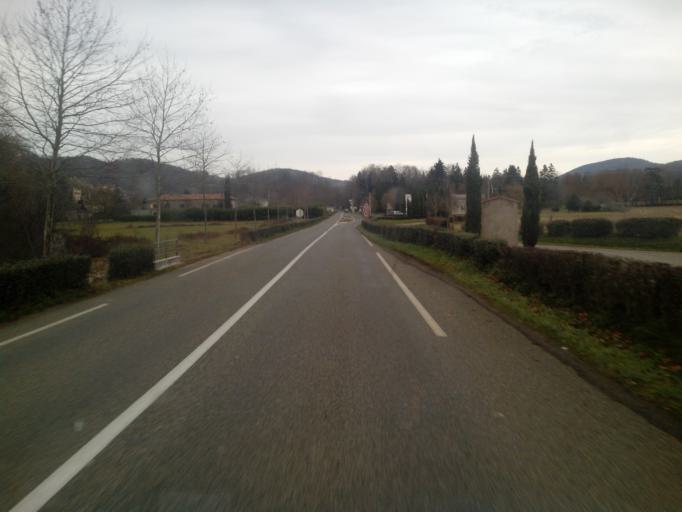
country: FR
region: Midi-Pyrenees
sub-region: Departement de l'Ariege
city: Foix
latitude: 43.0090
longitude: 1.4206
